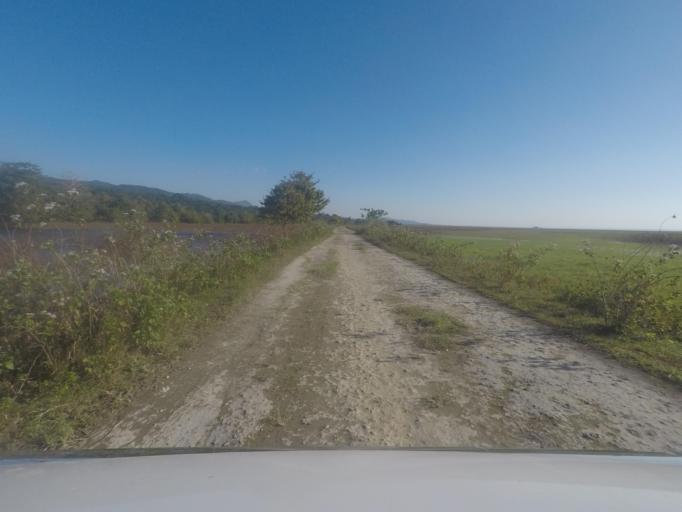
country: TL
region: Lautem
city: Lospalos
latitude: -8.4168
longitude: 127.1968
